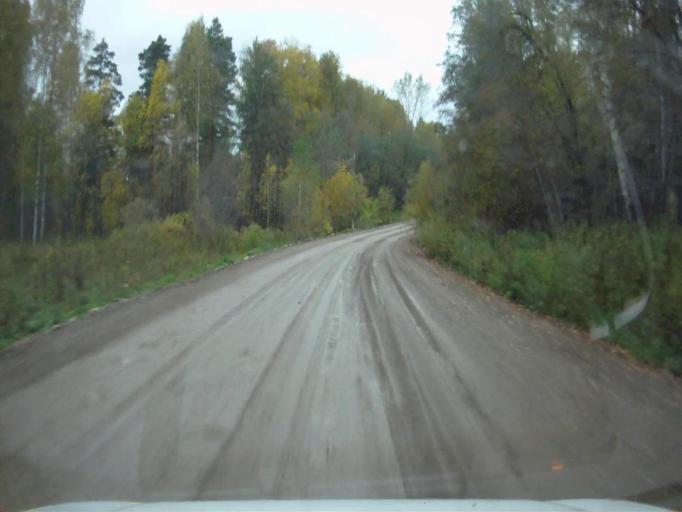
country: RU
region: Chelyabinsk
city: Nyazepetrovsk
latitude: 56.1010
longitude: 59.3890
